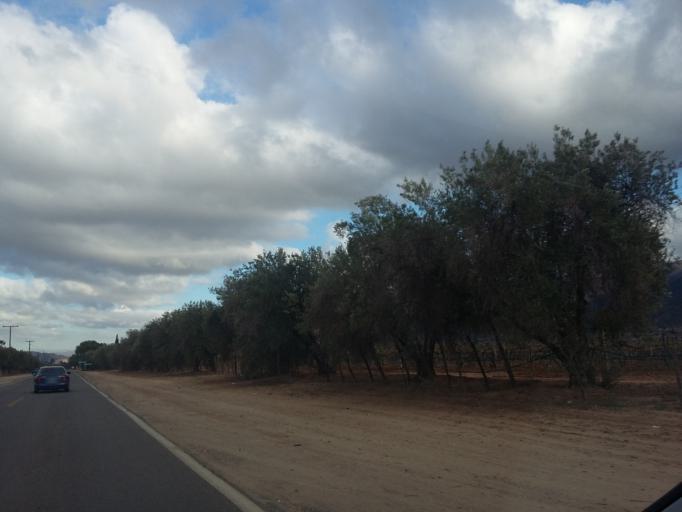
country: MX
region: Baja California
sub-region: Ensenada
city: Rancho Verde
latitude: 32.0883
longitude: -116.5912
